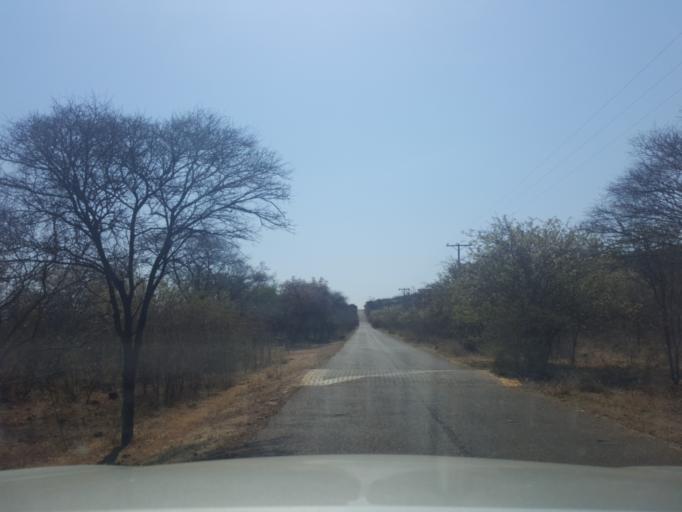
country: BW
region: Kweneng
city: Gabane
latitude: -24.7427
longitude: 25.8243
